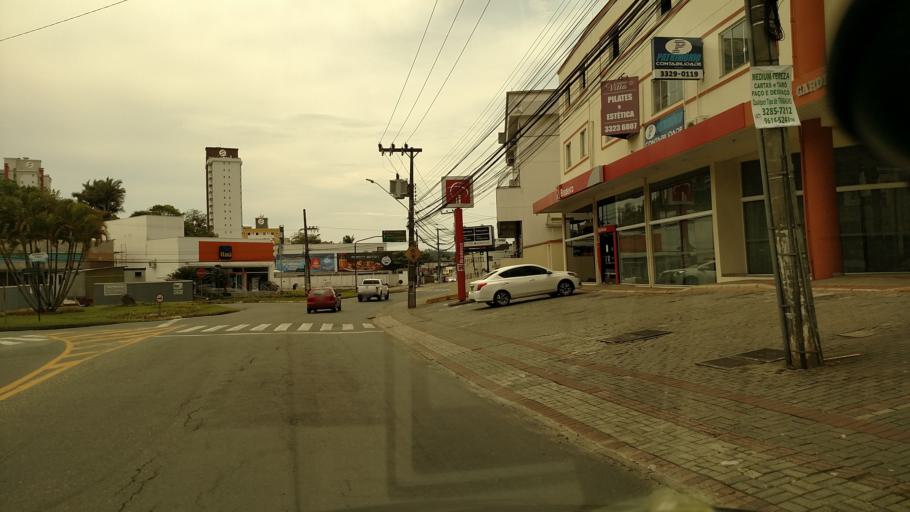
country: BR
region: Santa Catarina
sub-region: Blumenau
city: Blumenau
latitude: -26.9109
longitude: -49.0934
